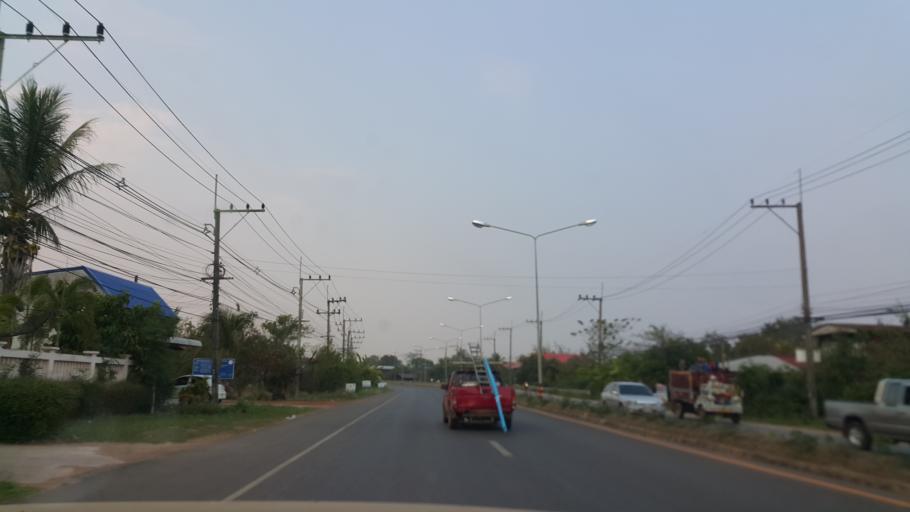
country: TH
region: Nakhon Phanom
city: That Phanom
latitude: 16.9820
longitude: 104.7278
